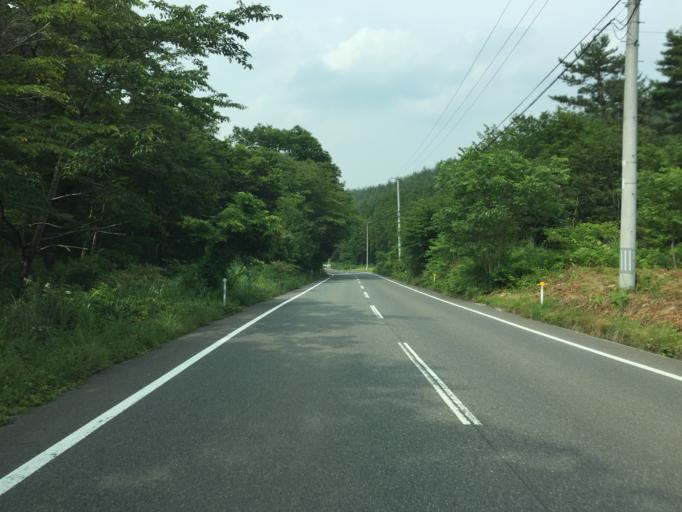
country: JP
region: Fukushima
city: Funehikimachi-funehiki
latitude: 37.4895
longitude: 140.7657
